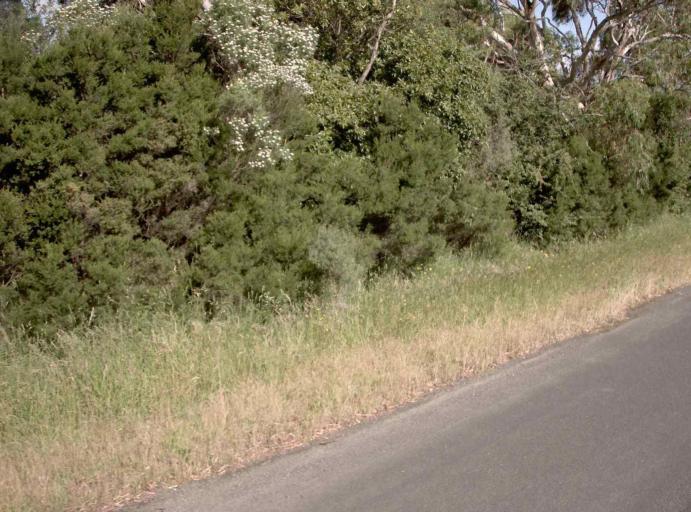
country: AU
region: Victoria
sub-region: Cardinia
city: Koo-Wee-Rup
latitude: -38.3646
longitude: 145.5631
